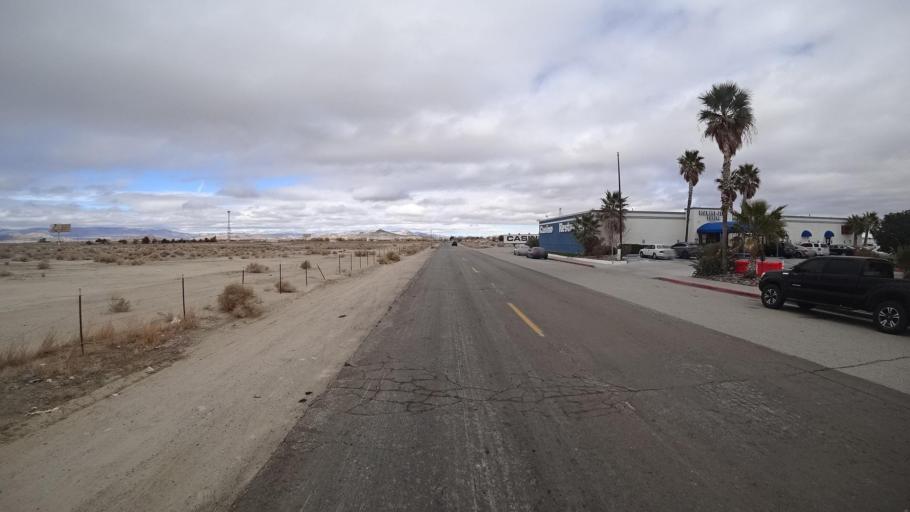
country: US
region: California
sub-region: Kern County
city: Rosamond
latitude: 34.8218
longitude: -118.1669
